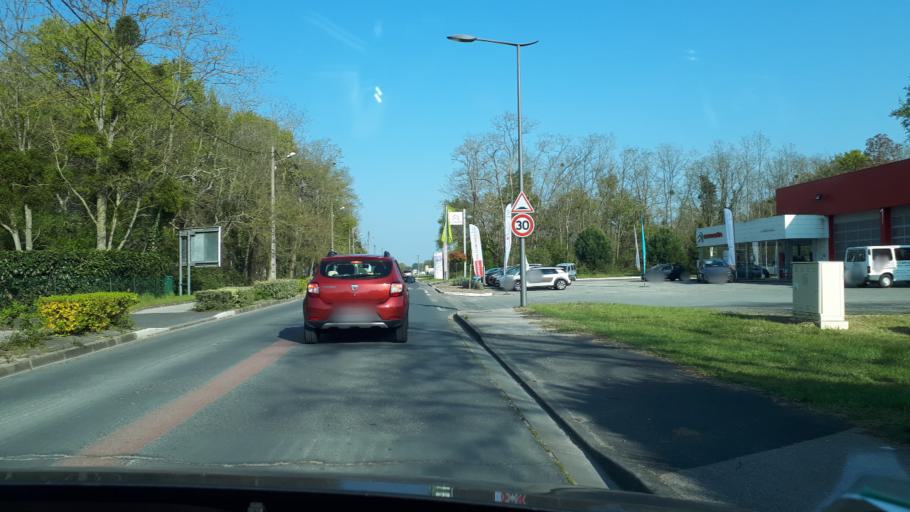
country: FR
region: Centre
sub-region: Departement d'Indre-et-Loire
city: Blere
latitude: 47.3244
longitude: 1.0113
